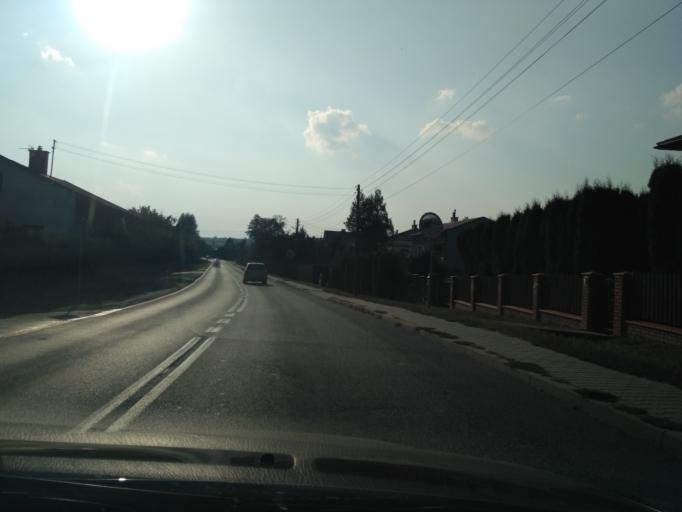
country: PL
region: Subcarpathian Voivodeship
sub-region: Powiat strzyzowski
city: Czudec
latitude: 49.9455
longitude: 21.8273
